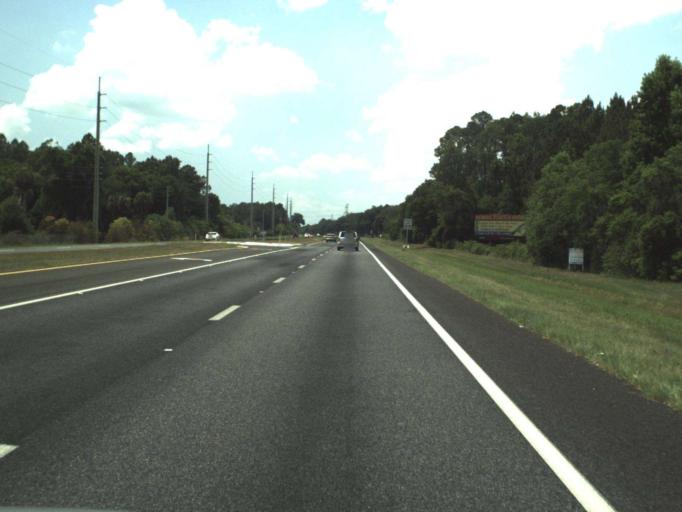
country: US
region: Florida
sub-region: Lake County
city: Fruitland Park
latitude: 28.8162
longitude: -81.9388
